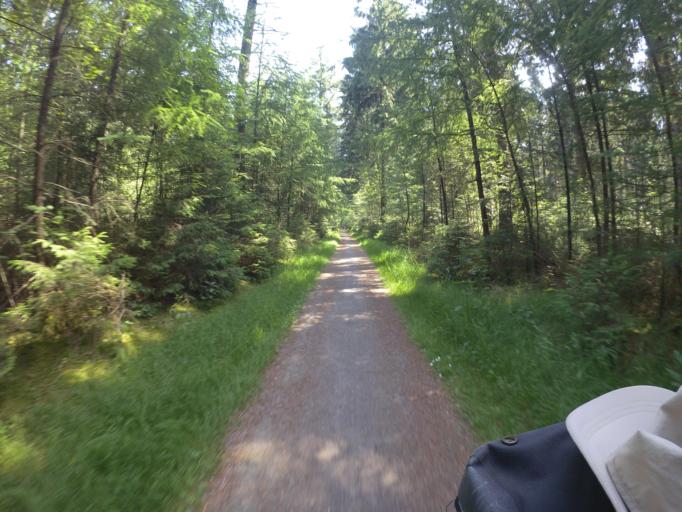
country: NL
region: Drenthe
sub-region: Gemeente De Wolden
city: Ruinen
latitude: 52.7290
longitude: 6.3717
